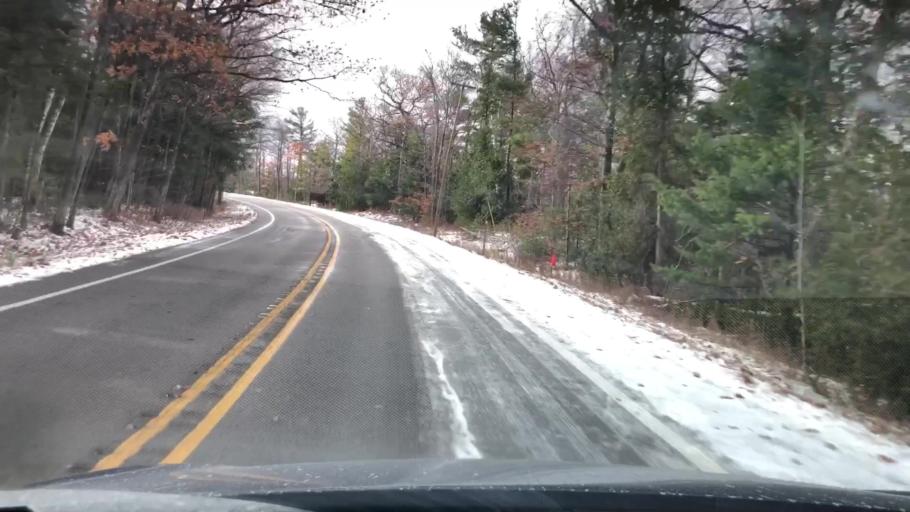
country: US
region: Michigan
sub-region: Antrim County
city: Elk Rapids
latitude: 44.9886
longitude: -85.4934
